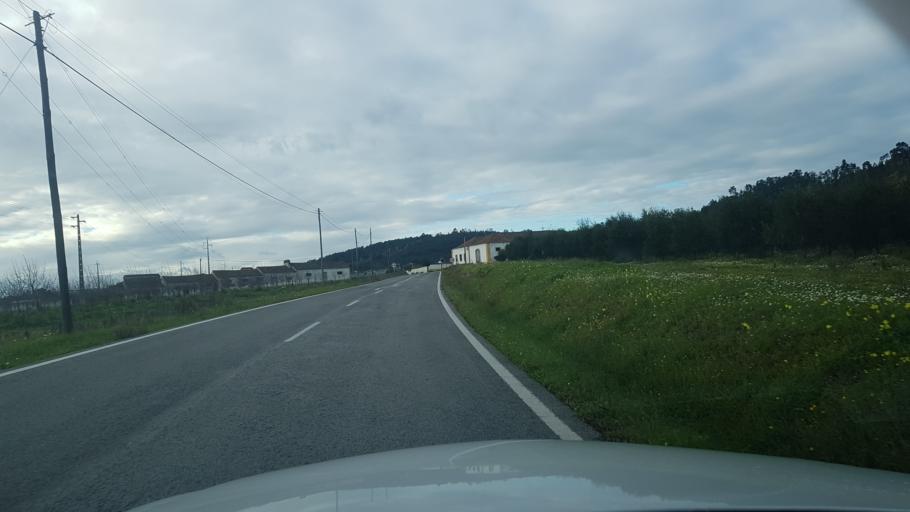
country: PT
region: Santarem
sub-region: Abrantes
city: Tramagal
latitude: 39.4844
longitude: -8.2601
